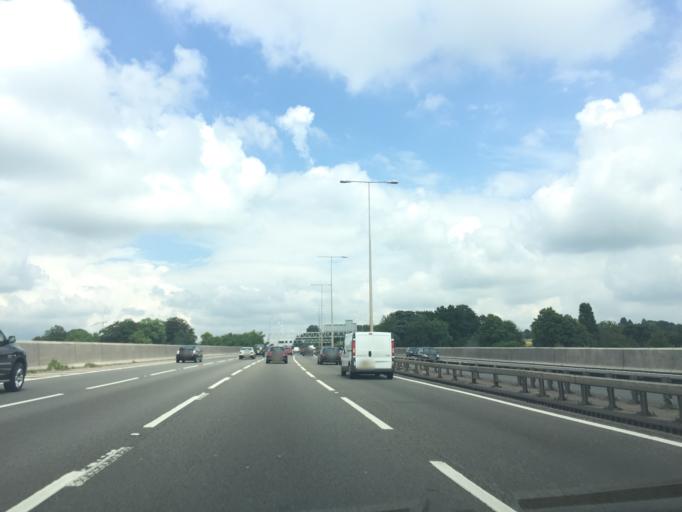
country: GB
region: England
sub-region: Hertfordshire
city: Kings Langley
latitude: 51.7041
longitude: -0.4394
